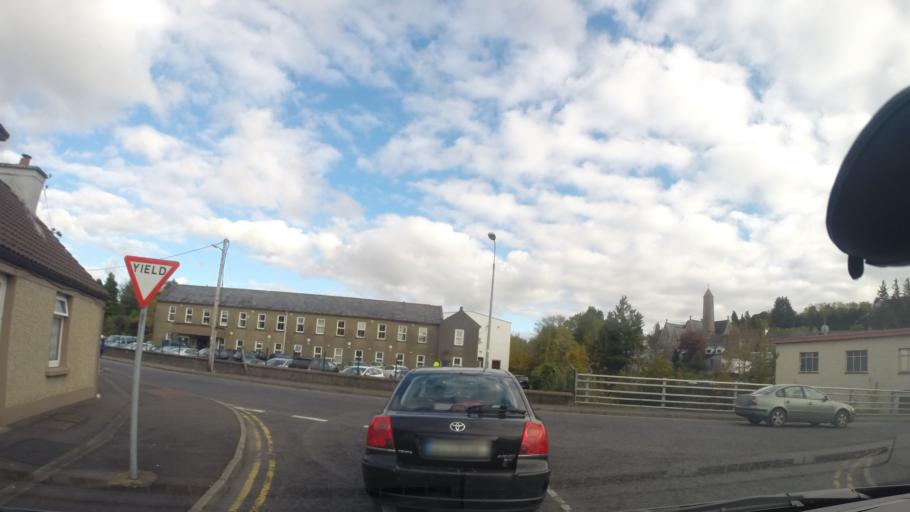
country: IE
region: Ulster
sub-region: County Donegal
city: Donegal
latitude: 54.6550
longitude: -8.1079
